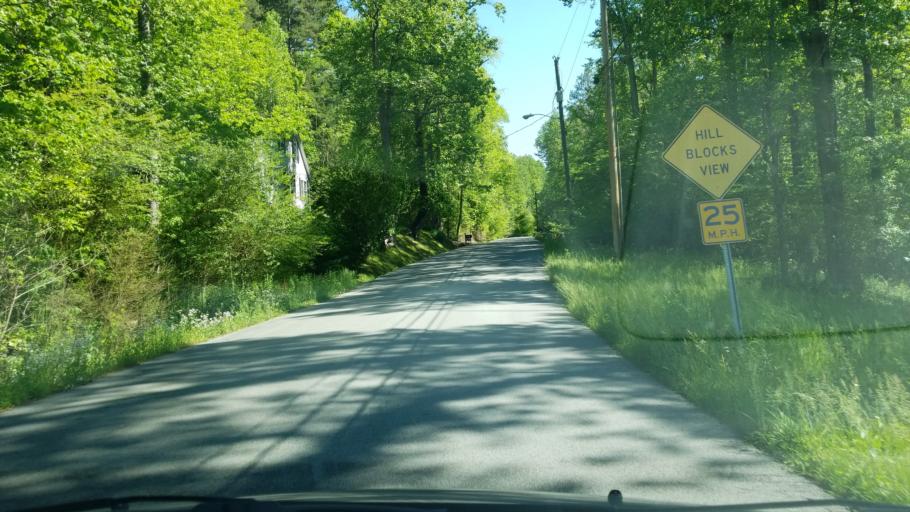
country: US
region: Tennessee
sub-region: Hamilton County
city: Walden
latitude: 35.1483
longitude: -85.2980
